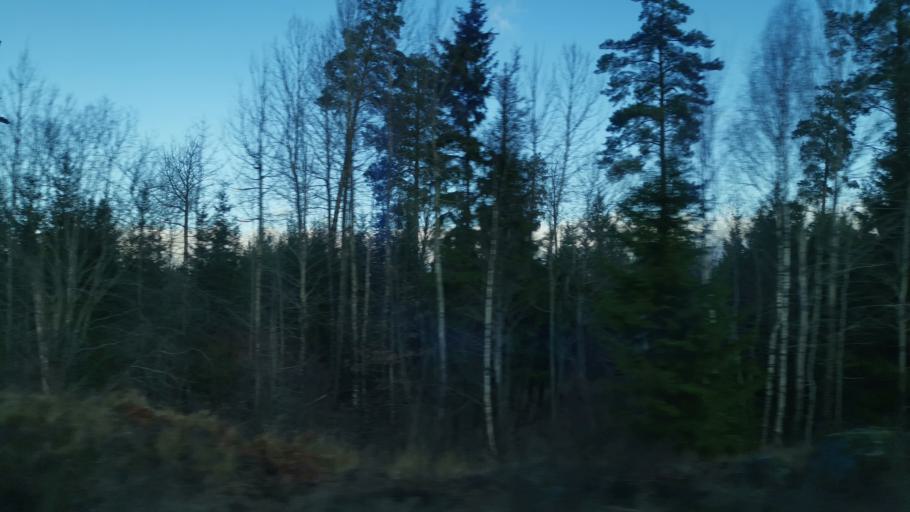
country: SE
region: Soedermanland
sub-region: Flens Kommun
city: Malmkoping
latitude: 59.0919
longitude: 16.9207
